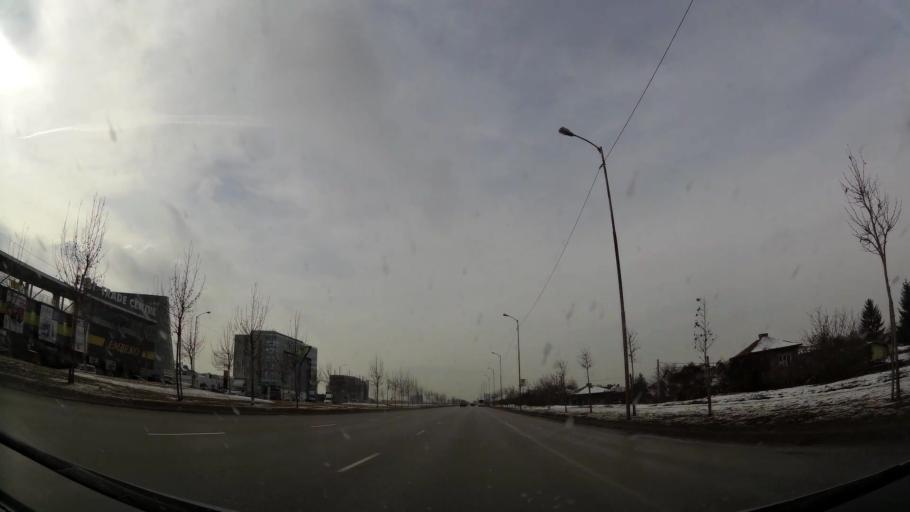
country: BG
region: Sofia-Capital
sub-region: Stolichna Obshtina
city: Sofia
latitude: 42.7078
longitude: 23.4116
